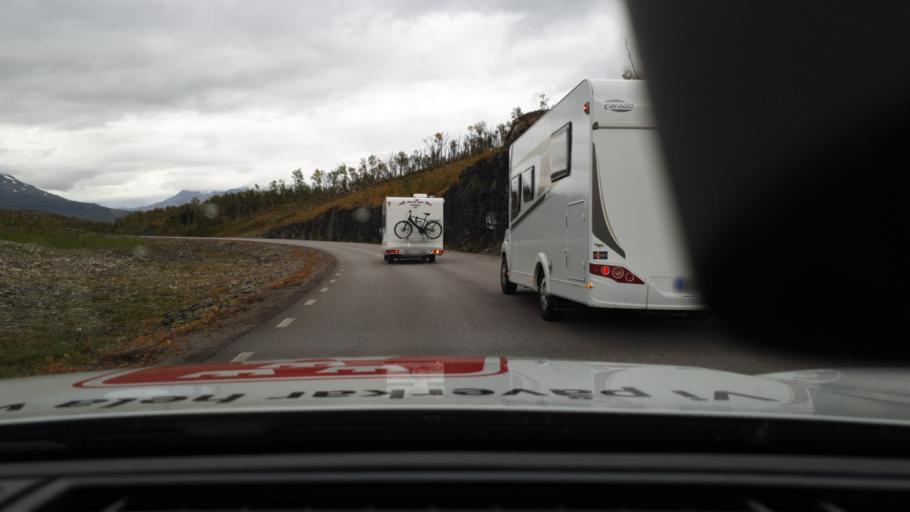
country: NO
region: Troms
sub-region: Bardu
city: Setermoen
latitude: 68.4345
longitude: 18.5877
